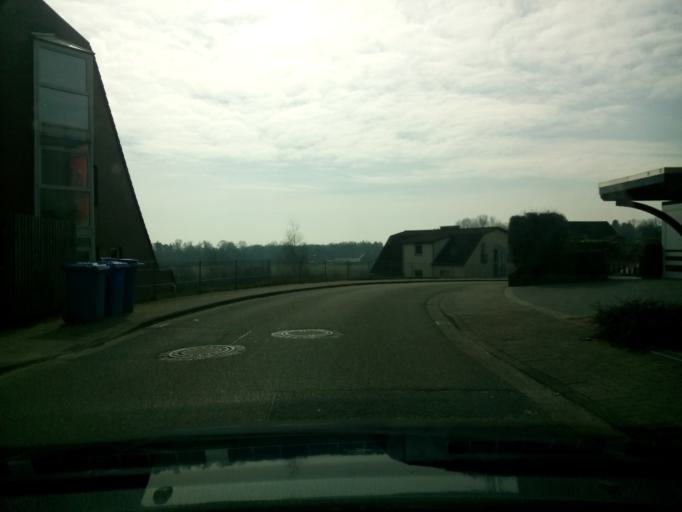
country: DE
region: Lower Saxony
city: Ritterhude
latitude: 53.2069
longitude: 8.7624
